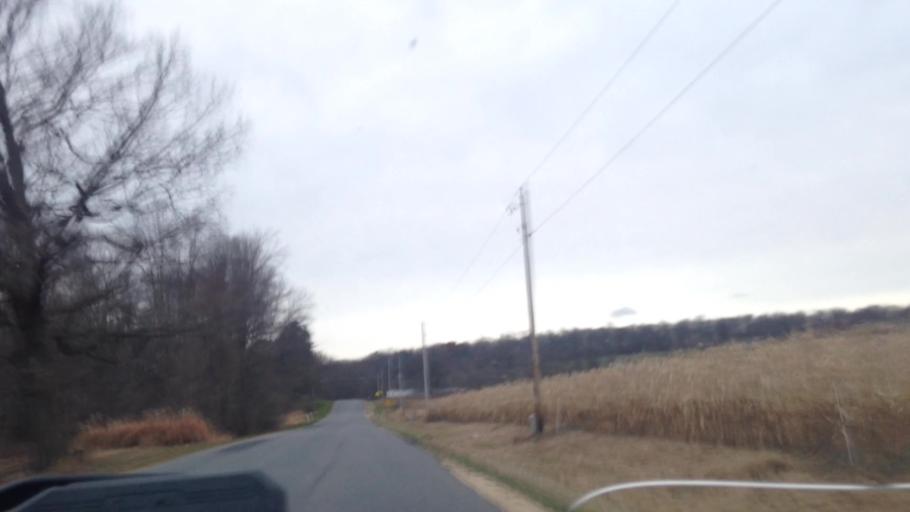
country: US
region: Wisconsin
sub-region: Dodge County
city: Theresa
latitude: 43.4862
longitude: -88.4925
